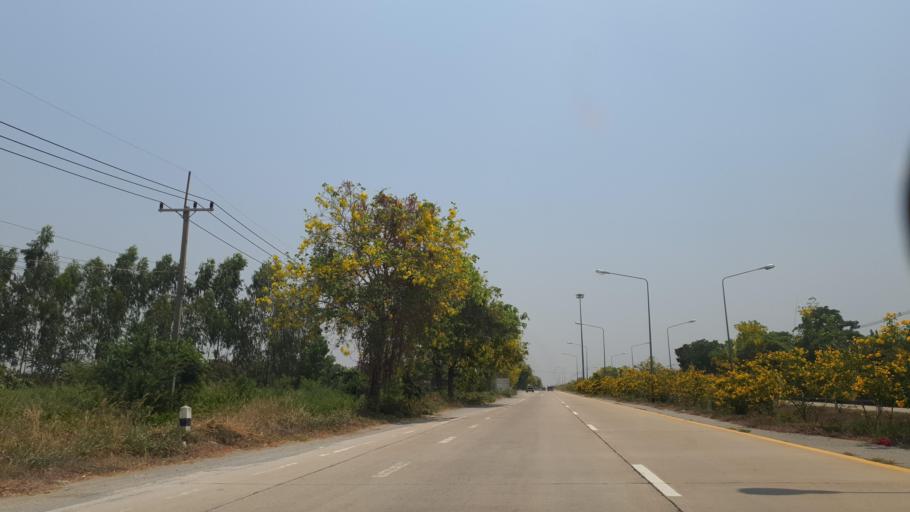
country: TH
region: Suphan Buri
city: Suphan Buri
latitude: 14.5404
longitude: 100.0686
